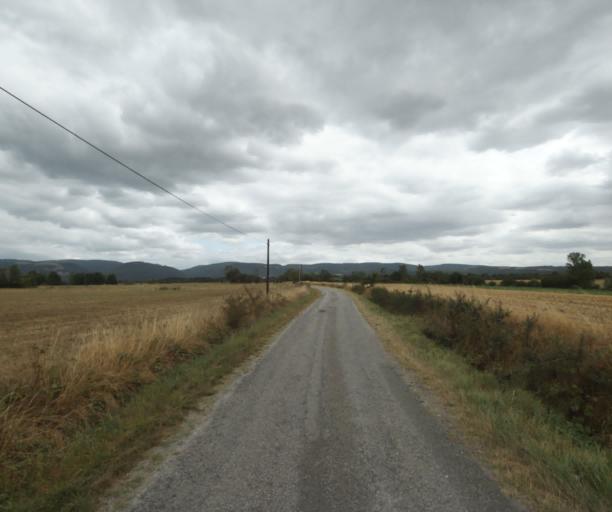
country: FR
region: Midi-Pyrenees
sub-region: Departement de la Haute-Garonne
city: Revel
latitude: 43.4821
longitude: 2.0299
